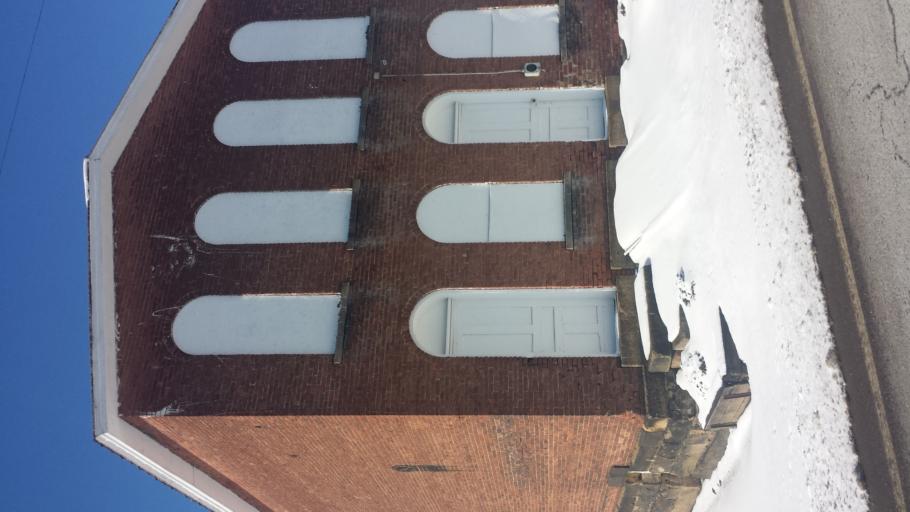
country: US
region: Ohio
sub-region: Carroll County
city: Carrollton
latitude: 40.4646
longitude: -81.0022
